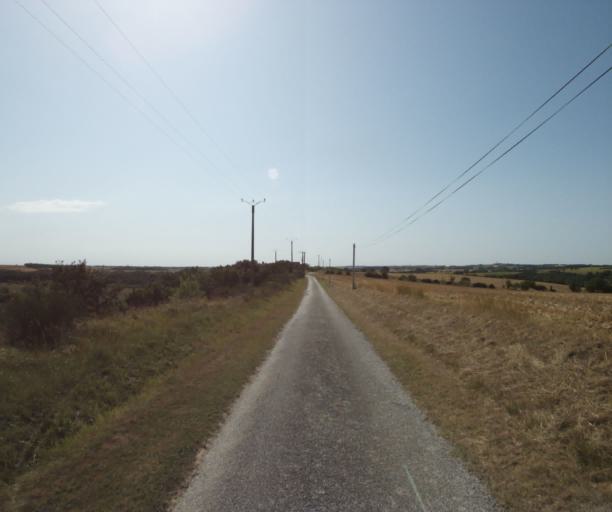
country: FR
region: Midi-Pyrenees
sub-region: Departement de la Haute-Garonne
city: Saint-Felix-Lauragais
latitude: 43.4409
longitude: 1.8299
